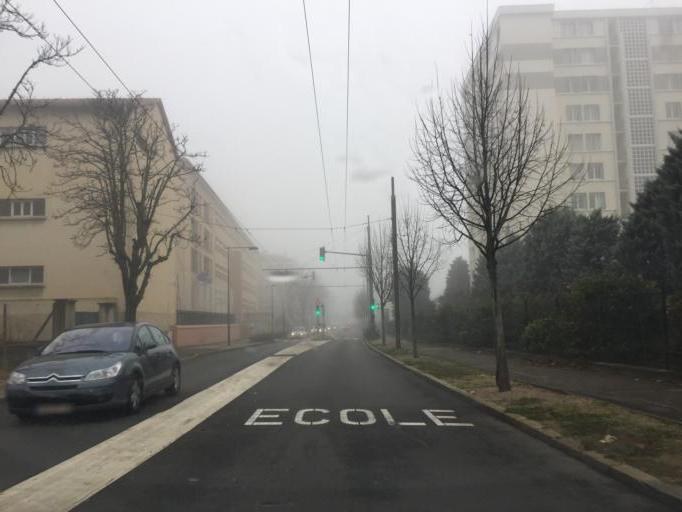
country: FR
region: Rhone-Alpes
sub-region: Departement du Rhone
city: Caluire-et-Cuire
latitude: 45.7938
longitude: 4.8459
